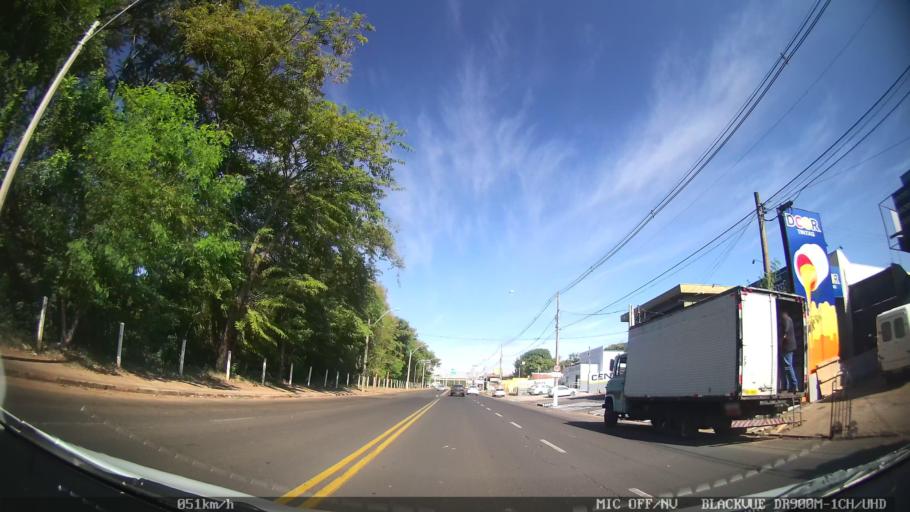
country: BR
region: Sao Paulo
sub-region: Sao Jose Do Rio Preto
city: Sao Jose do Rio Preto
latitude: -20.7873
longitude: -49.3868
